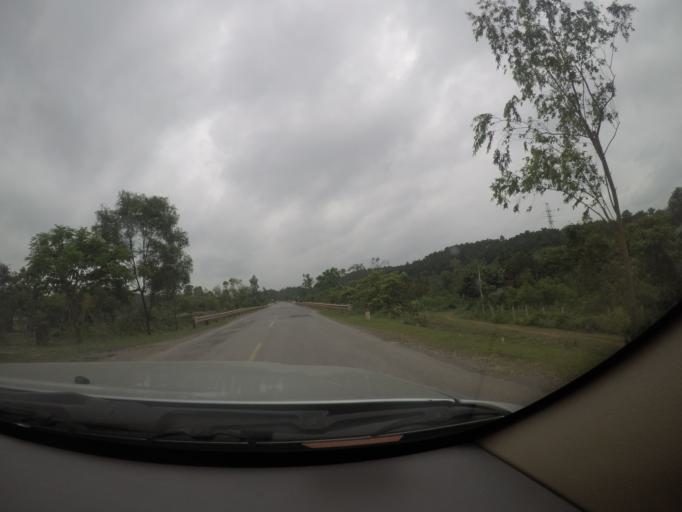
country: VN
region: Quang Binh
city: Quan Hau
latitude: 17.3601
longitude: 106.6230
